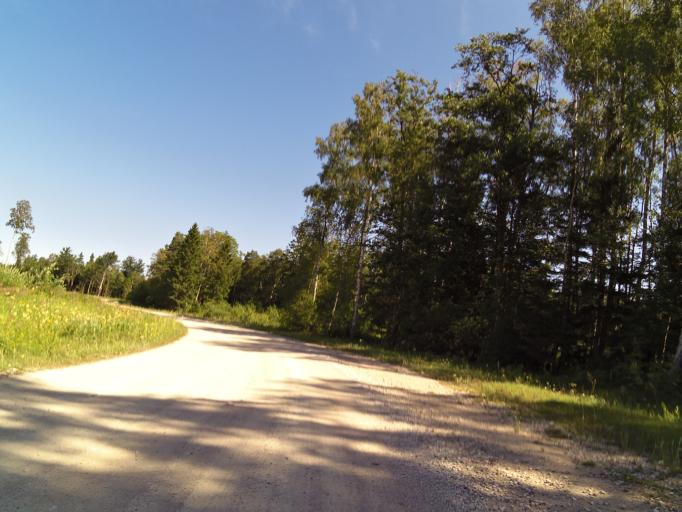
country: EE
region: Hiiumaa
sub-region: Kaerdla linn
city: Kardla
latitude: 58.9268
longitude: 22.3689
